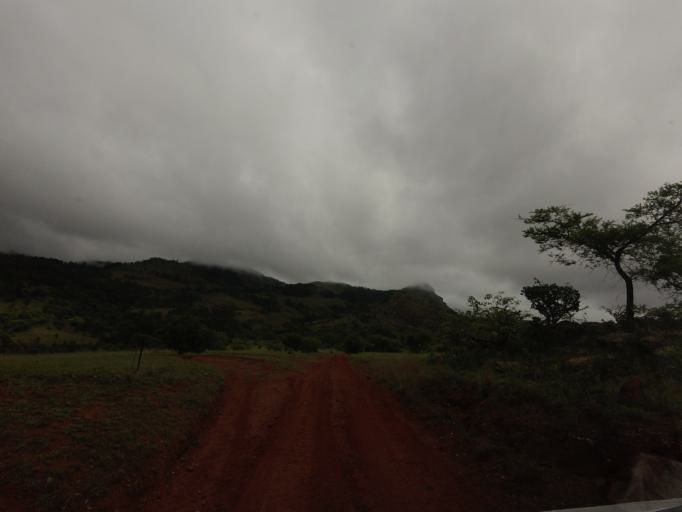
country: SZ
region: Hhohho
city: Lobamba
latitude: -26.4691
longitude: 31.1773
